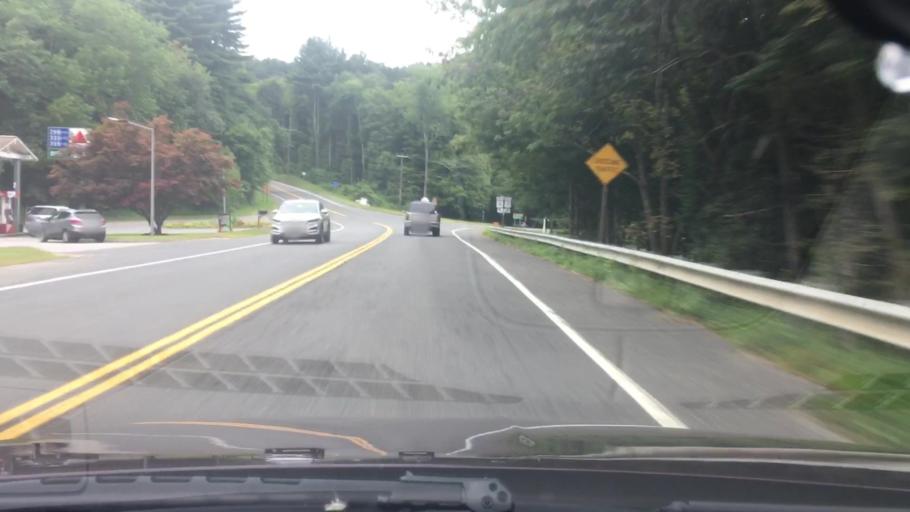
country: US
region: Connecticut
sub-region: Litchfield County
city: Kent
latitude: 41.8203
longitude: -73.3740
